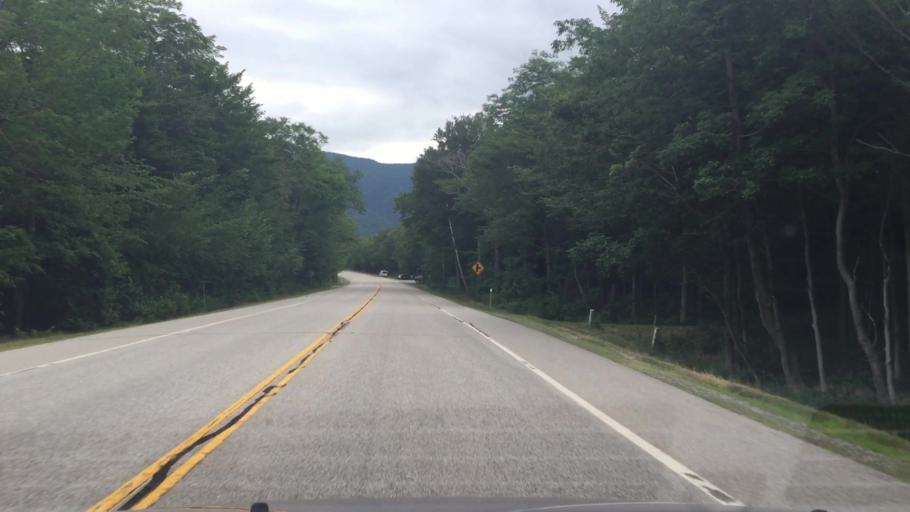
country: US
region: New Hampshire
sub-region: Grafton County
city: Deerfield
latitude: 44.1717
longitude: -71.3909
